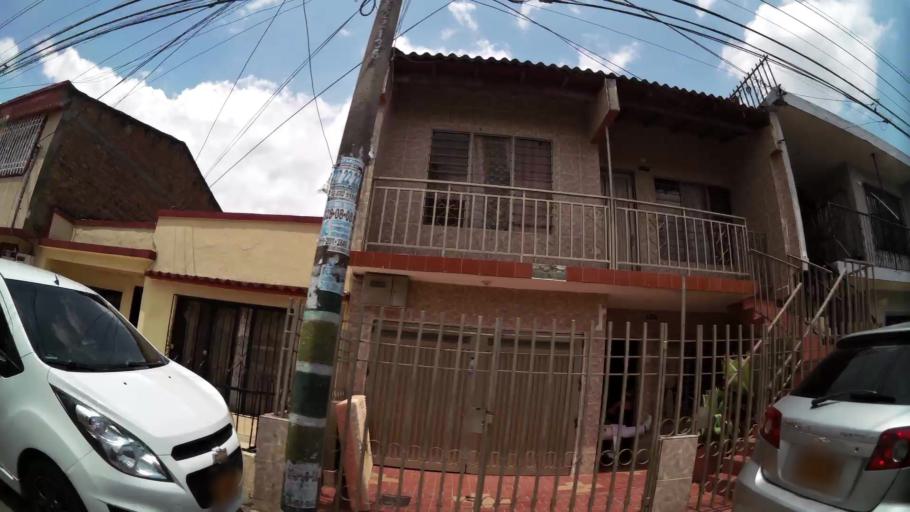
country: CO
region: Valle del Cauca
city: Cali
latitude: 3.4528
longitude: -76.4789
